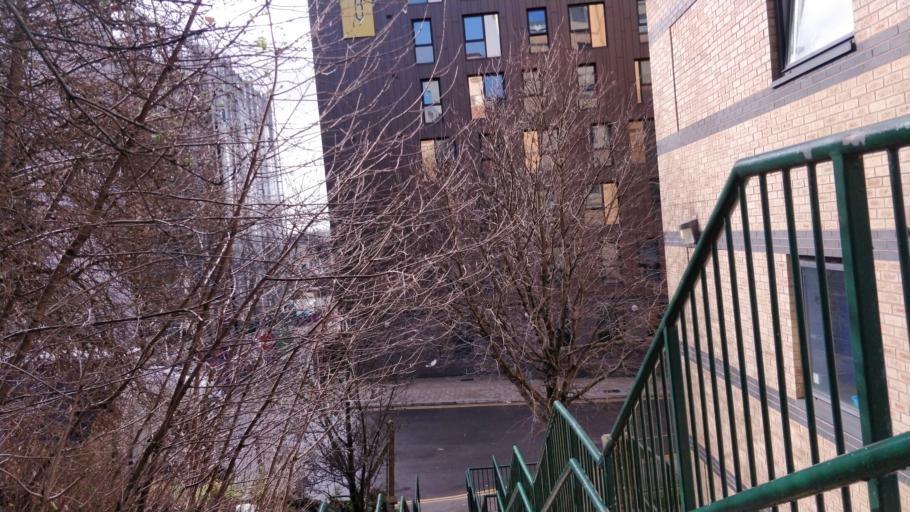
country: GB
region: England
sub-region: City and Borough of Leeds
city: Leeds
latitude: 53.8002
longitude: -1.5621
